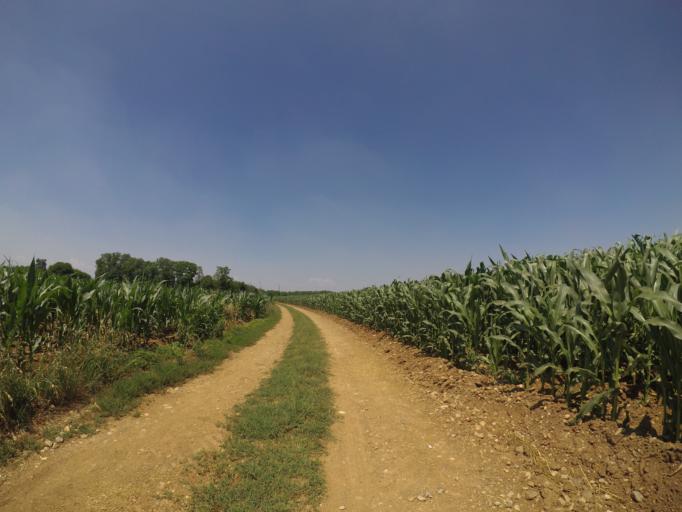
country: IT
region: Friuli Venezia Giulia
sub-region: Provincia di Udine
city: Bertiolo
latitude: 45.9471
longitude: 13.0286
